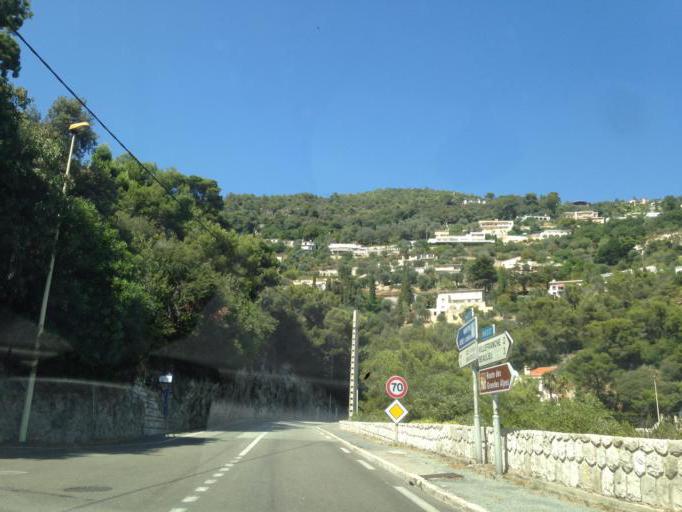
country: FR
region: Provence-Alpes-Cote d'Azur
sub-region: Departement des Alpes-Maritimes
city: Beaulieu-sur-Mer
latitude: 43.7123
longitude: 7.3200
